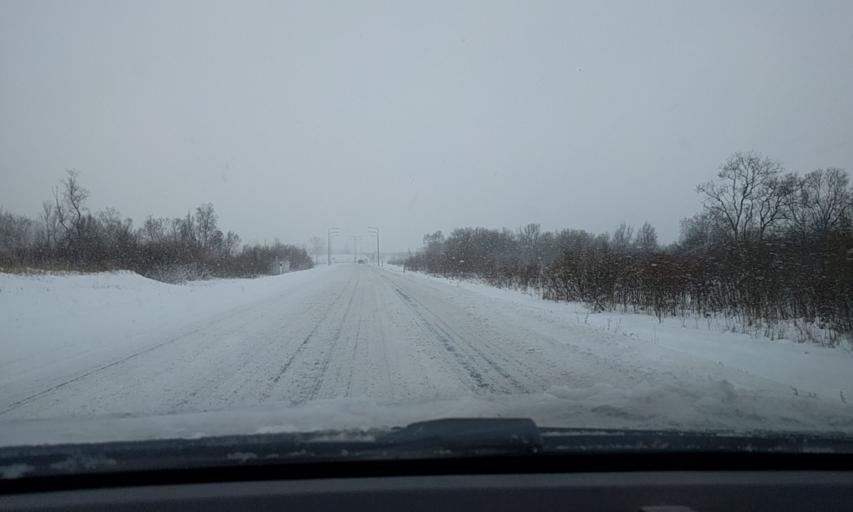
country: EE
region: Harju
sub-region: Joelaehtme vald
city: Loo
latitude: 59.4608
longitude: 24.9812
